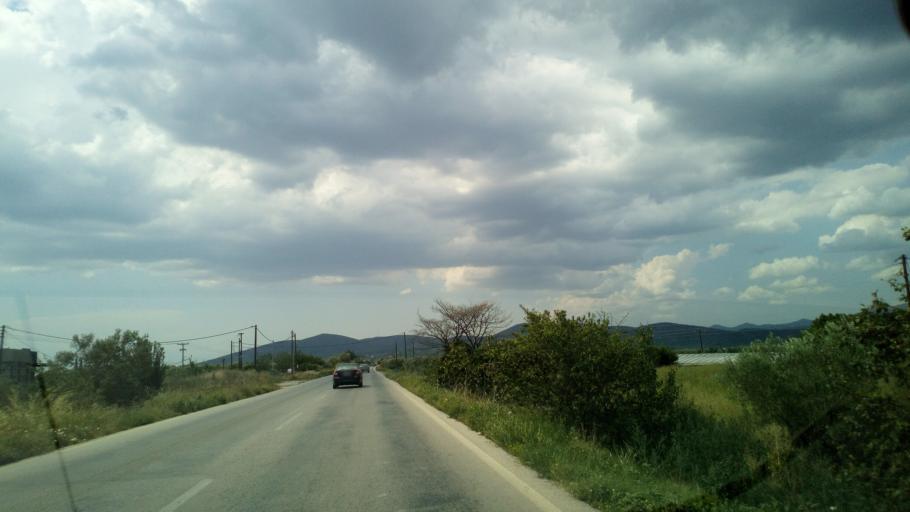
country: GR
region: Central Macedonia
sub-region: Nomos Chalkidikis
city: Ormylia
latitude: 40.2557
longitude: 23.5400
